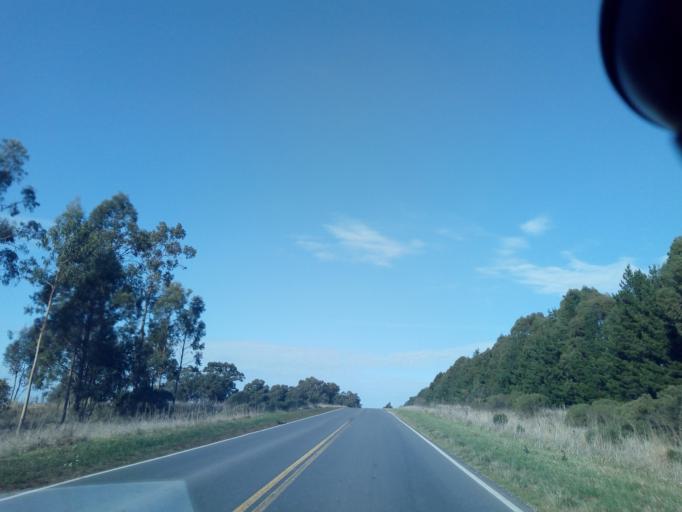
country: AR
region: Buenos Aires
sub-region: Partido de Tandil
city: Tandil
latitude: -37.3516
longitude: -58.8868
